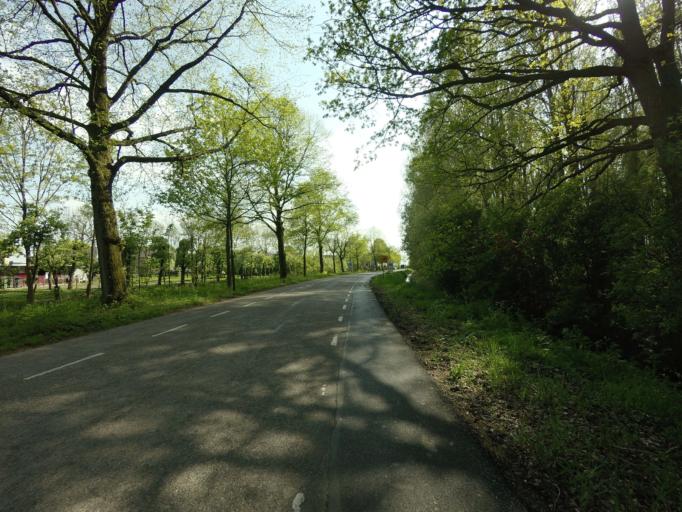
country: NL
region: Utrecht
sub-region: Gemeente Houten
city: Houten
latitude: 51.9984
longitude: 5.1788
